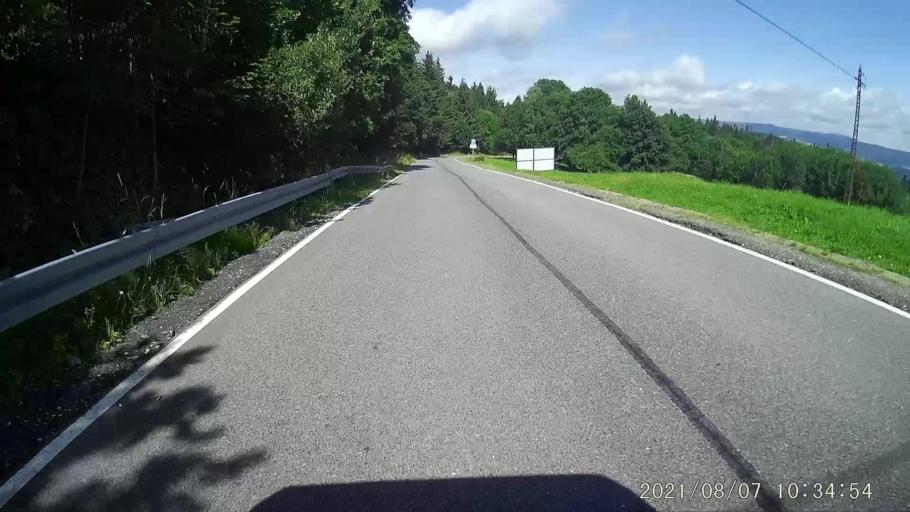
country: PL
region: Lower Silesian Voivodeship
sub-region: Powiat klodzki
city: Duszniki-Zdroj
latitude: 50.3709
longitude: 16.3660
